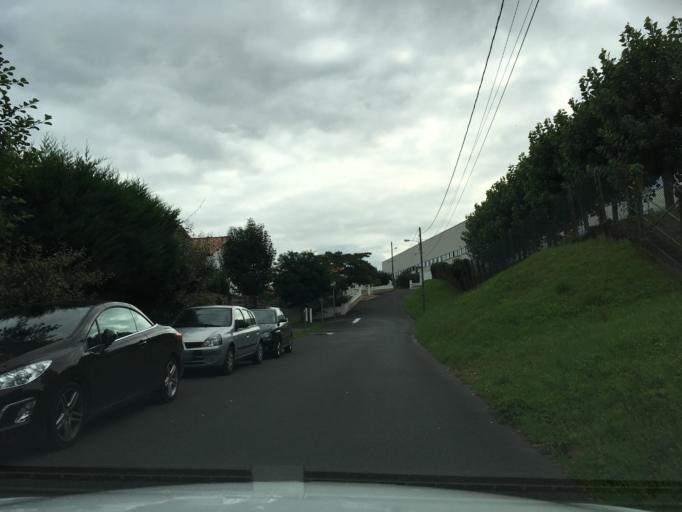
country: FR
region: Aquitaine
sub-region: Departement des Pyrenees-Atlantiques
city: Bayonne
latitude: 43.5024
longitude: -1.5028
